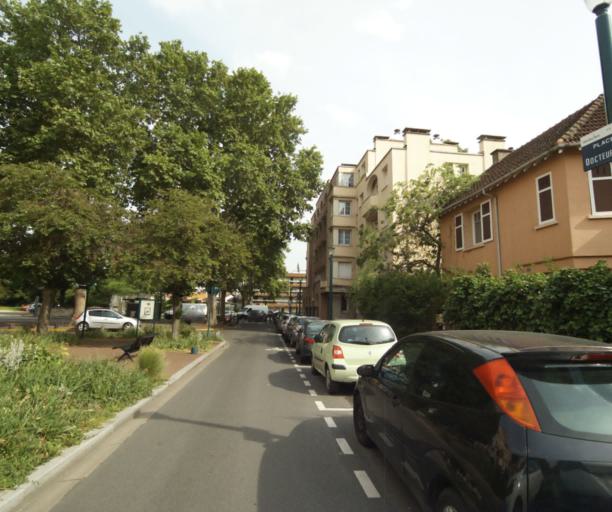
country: FR
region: Ile-de-France
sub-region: Departement des Hauts-de-Seine
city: Gennevilliers
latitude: 48.9275
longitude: 2.2941
